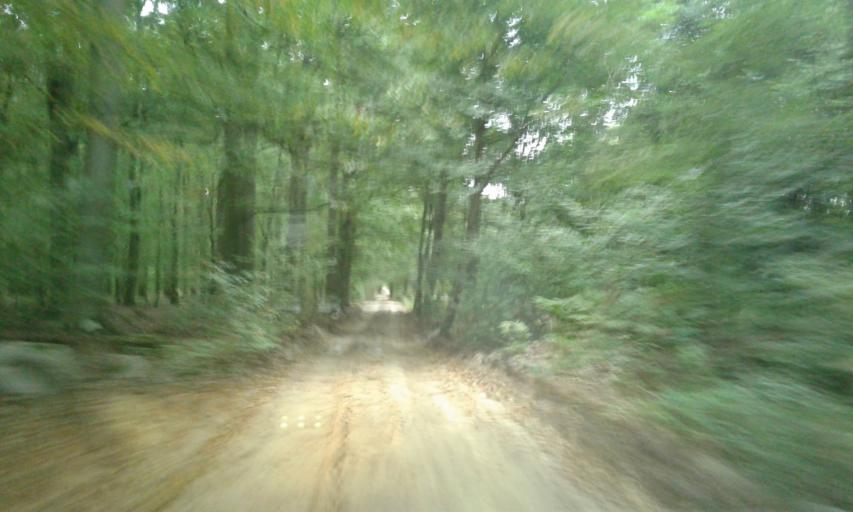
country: PL
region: West Pomeranian Voivodeship
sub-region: Powiat stargardzki
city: Dolice
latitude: 53.1781
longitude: 15.2496
